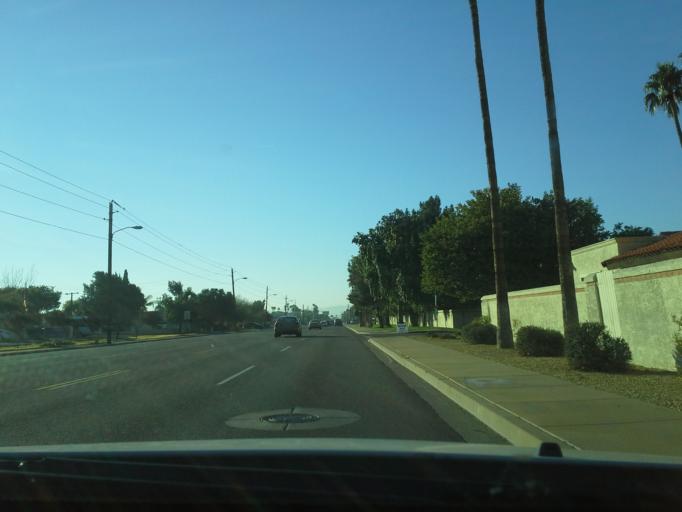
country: US
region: Arizona
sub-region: Maricopa County
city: Phoenix
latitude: 33.5430
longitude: -112.0652
